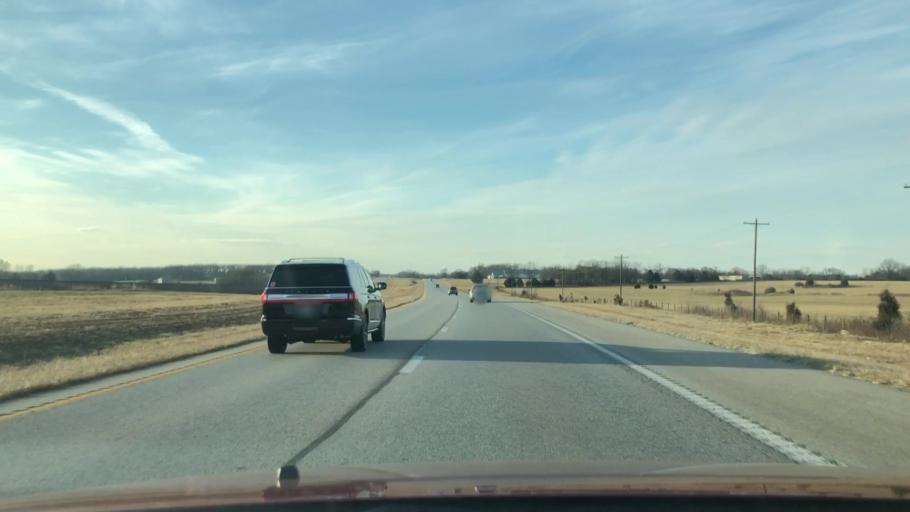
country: US
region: Missouri
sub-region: Webster County
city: Seymour
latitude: 37.1242
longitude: -92.7020
